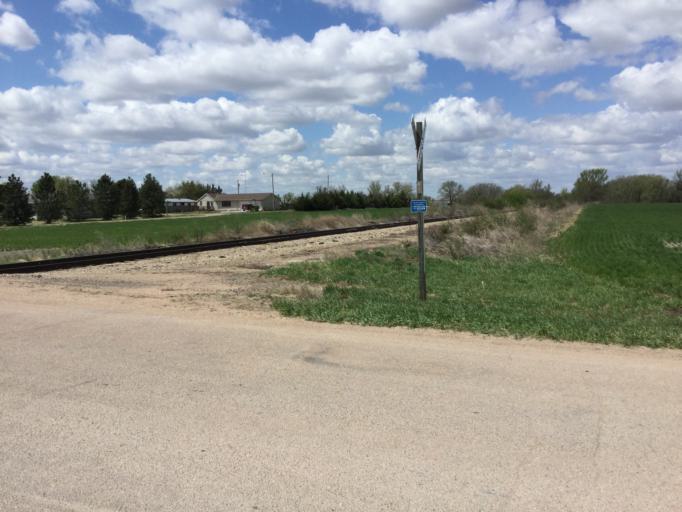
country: US
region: Kansas
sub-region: Phillips County
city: Phillipsburg
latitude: 39.7640
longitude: -99.1229
